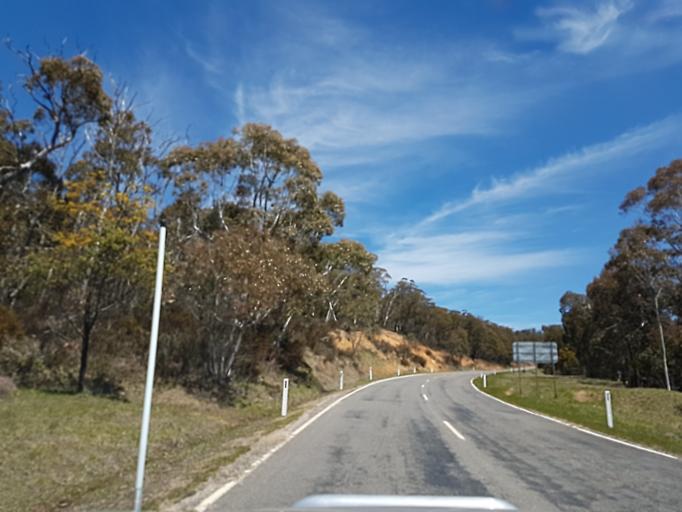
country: AU
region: Victoria
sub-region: Alpine
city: Mount Beauty
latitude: -37.0815
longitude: 147.3822
